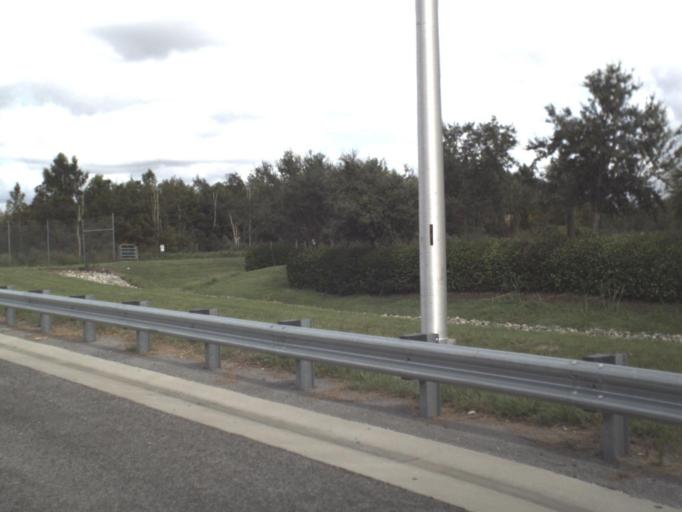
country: US
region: Florida
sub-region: Lee County
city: Villas
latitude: 26.5176
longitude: -81.8535
